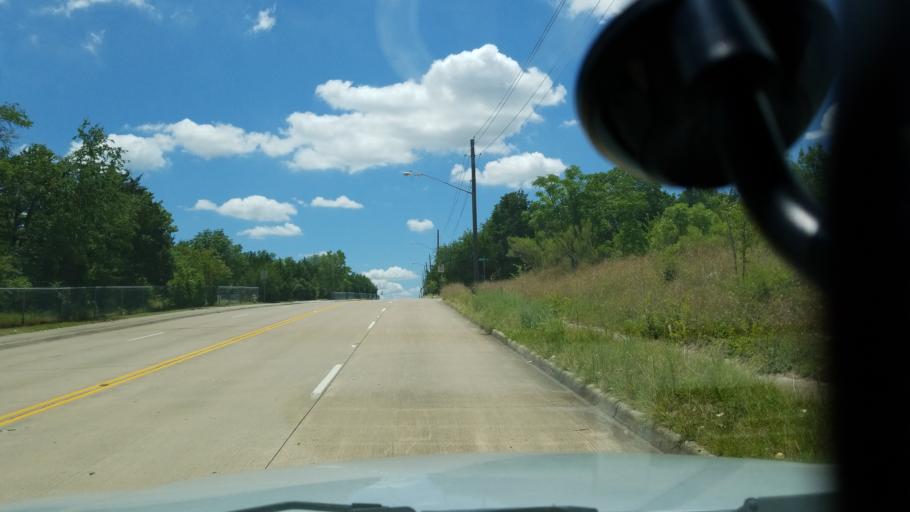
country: US
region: Texas
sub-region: Dallas County
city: Duncanville
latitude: 32.6696
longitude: -96.8743
